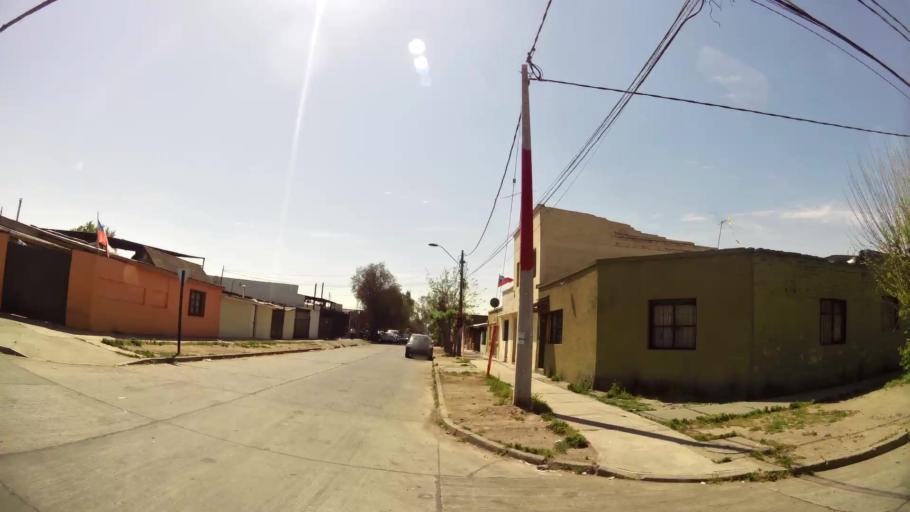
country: CL
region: Santiago Metropolitan
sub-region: Provincia de Santiago
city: La Pintana
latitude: -33.5336
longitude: -70.6476
